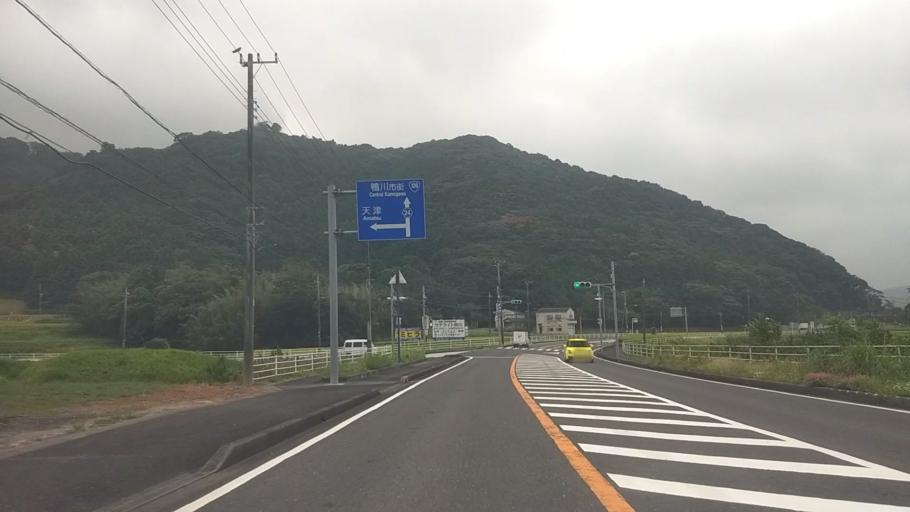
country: JP
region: Chiba
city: Kawaguchi
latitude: 35.1332
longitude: 140.0781
